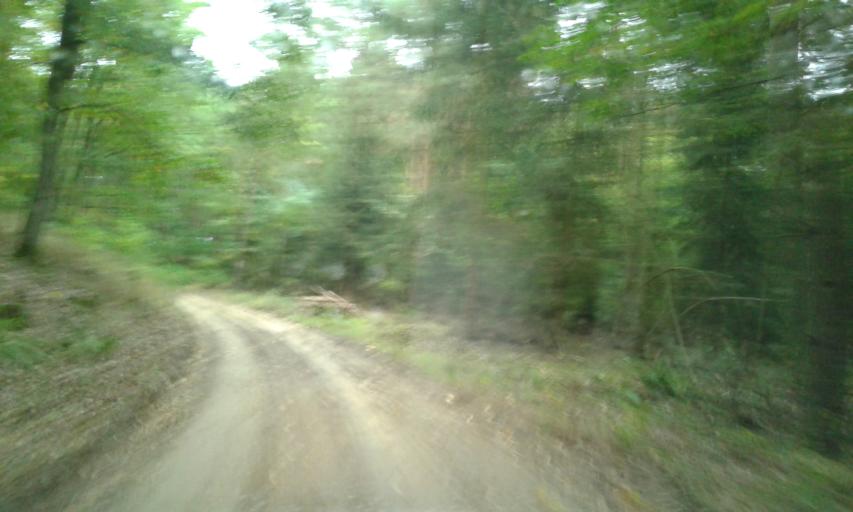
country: PL
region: West Pomeranian Voivodeship
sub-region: Powiat choszczenski
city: Pelczyce
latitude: 53.0894
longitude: 15.2313
